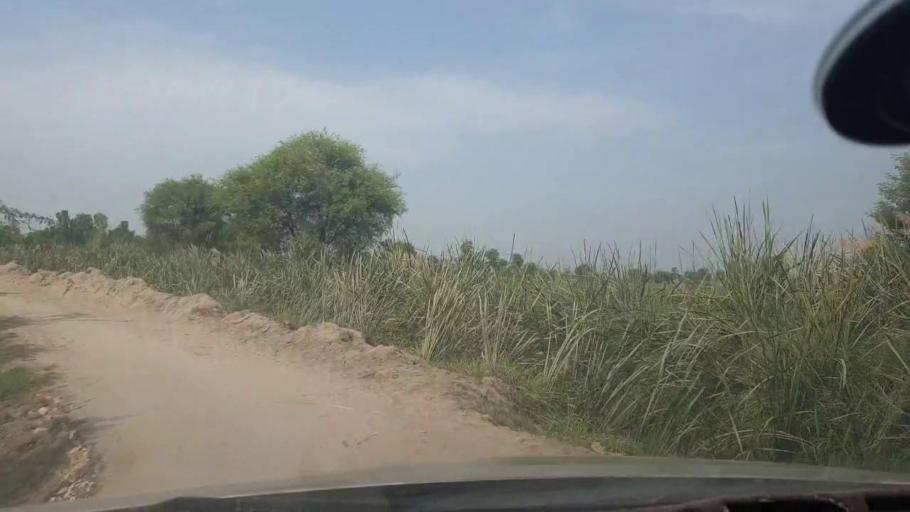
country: PK
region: Sindh
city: Jacobabad
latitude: 28.3118
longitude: 68.4756
